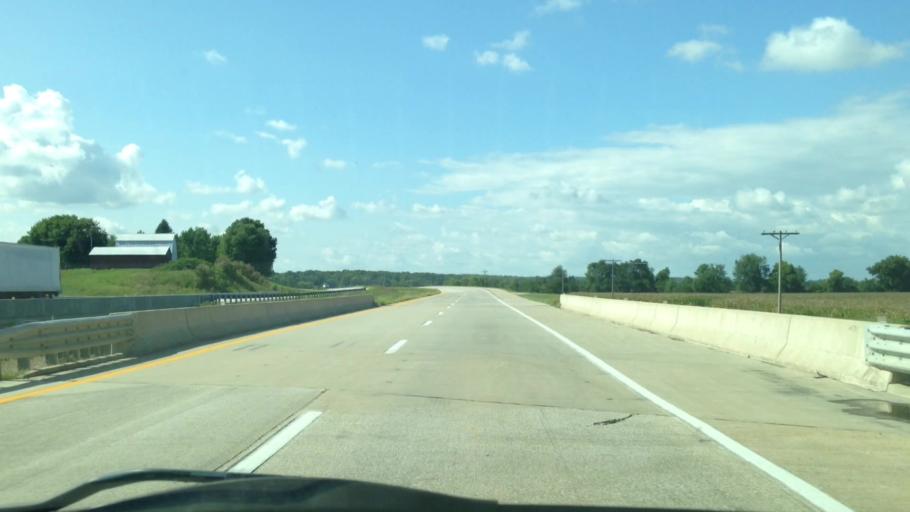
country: US
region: Illinois
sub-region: Hancock County
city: Warsaw
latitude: 40.2678
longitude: -91.5533
